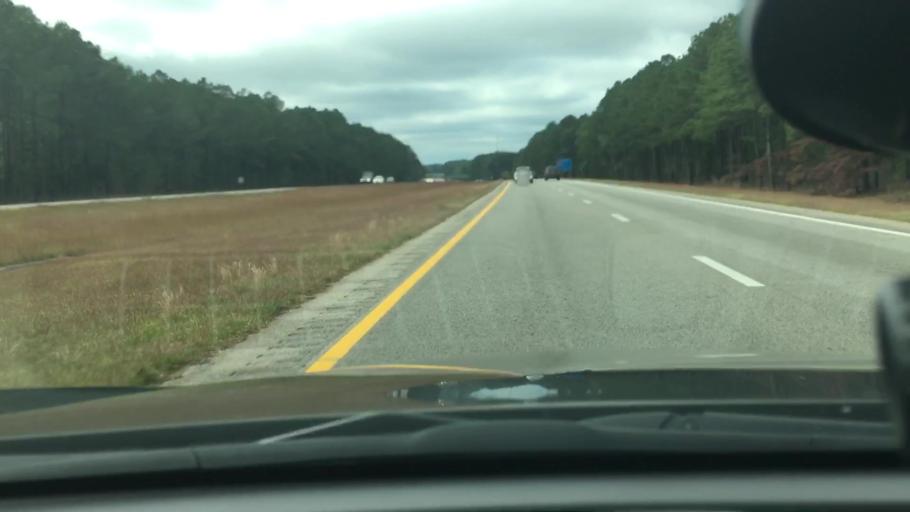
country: US
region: North Carolina
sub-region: Nash County
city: Spring Hope
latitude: 35.7869
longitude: -78.1055
